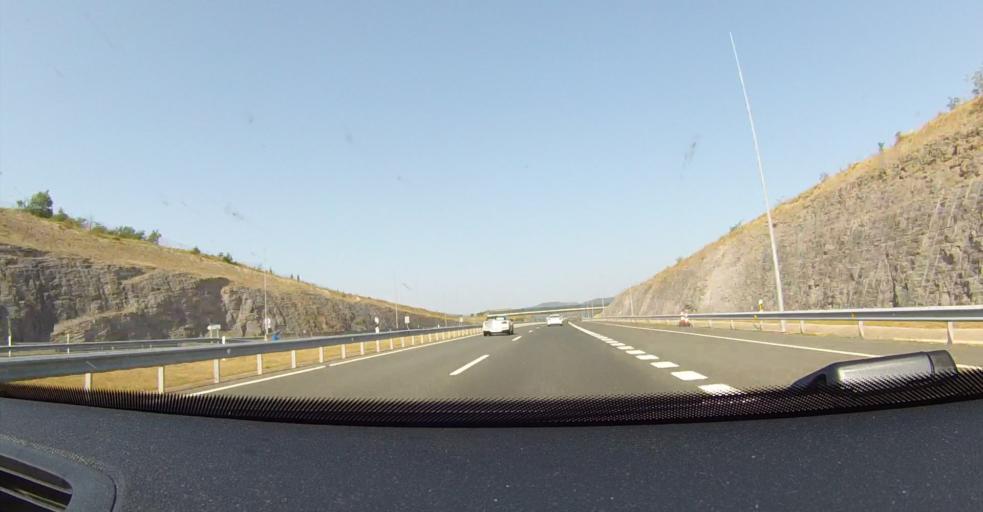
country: ES
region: Basque Country
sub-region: Provincia de Alava
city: Gasteiz / Vitoria
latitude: 42.9183
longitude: -2.6780
